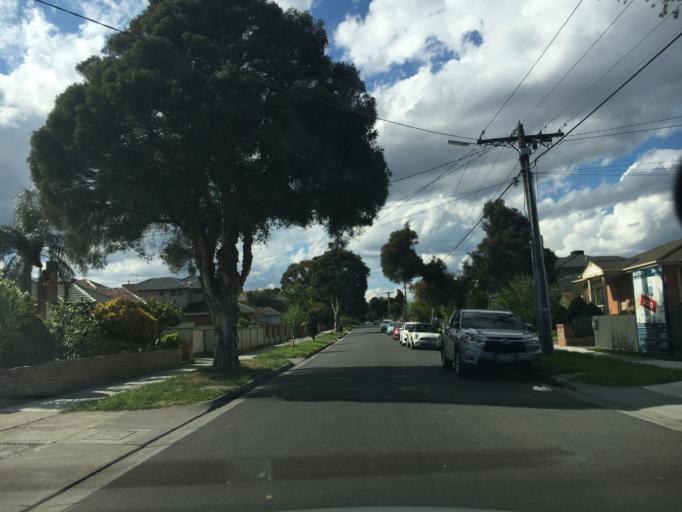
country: AU
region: Victoria
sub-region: Monash
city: Clayton
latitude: -37.9290
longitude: 145.1291
